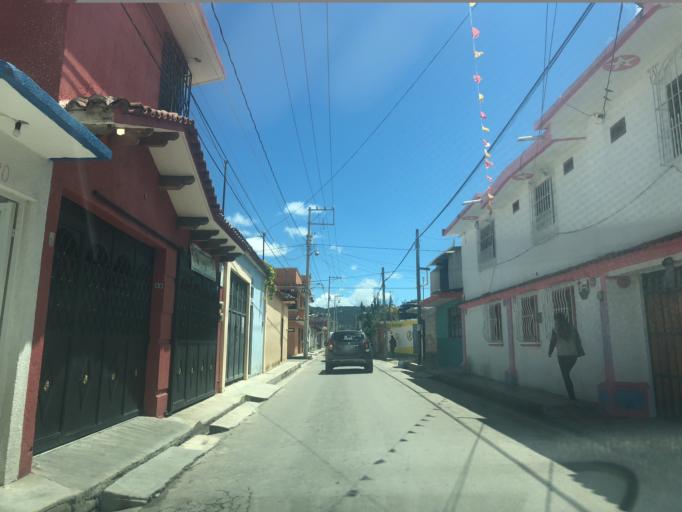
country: MX
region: Chiapas
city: San Cristobal de las Casas
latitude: 16.7174
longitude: -92.6424
